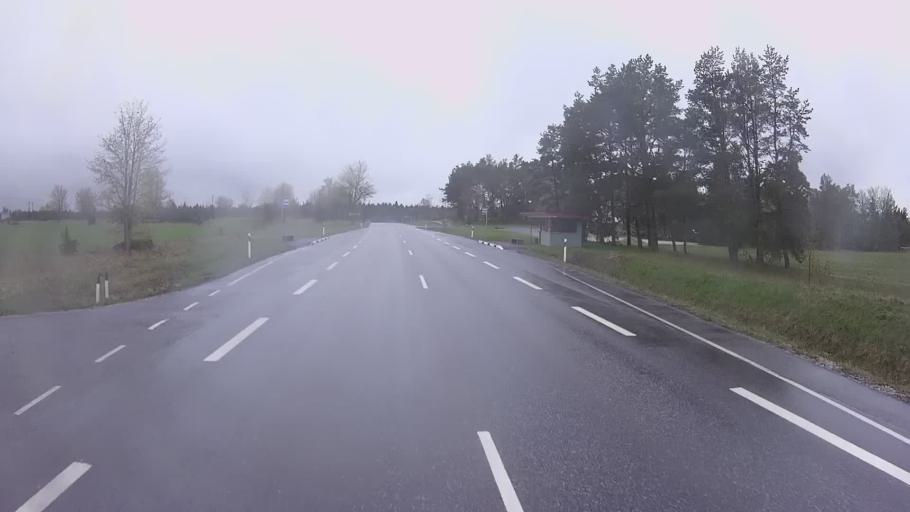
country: EE
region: Hiiumaa
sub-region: Kaerdla linn
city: Kardla
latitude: 58.9838
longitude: 22.5118
